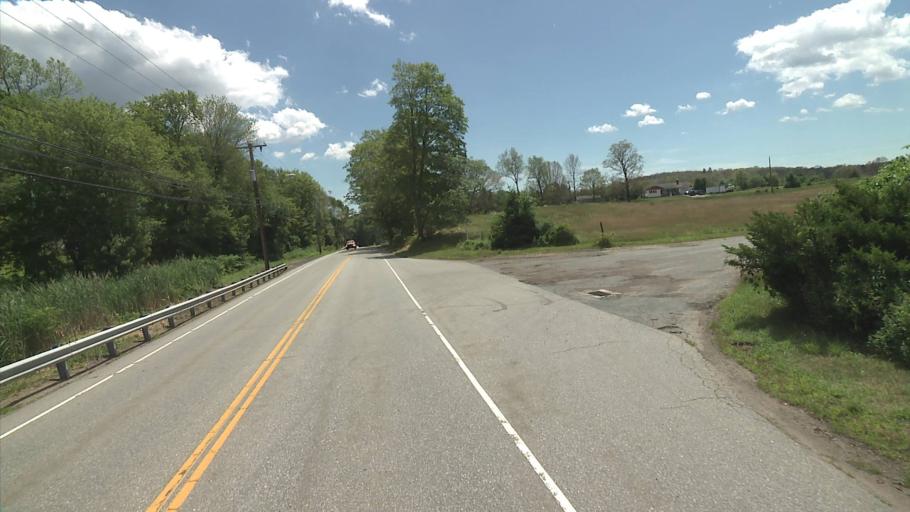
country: US
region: Connecticut
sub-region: Middlesex County
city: Moodus
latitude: 41.5054
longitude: -72.4765
